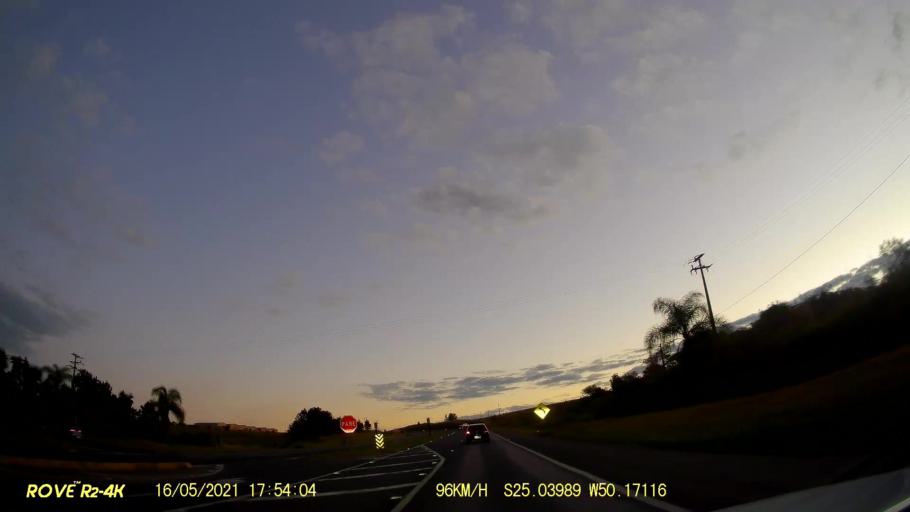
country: BR
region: Parana
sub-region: Ponta Grossa
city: Ponta Grossa
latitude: -25.0398
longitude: -50.1710
